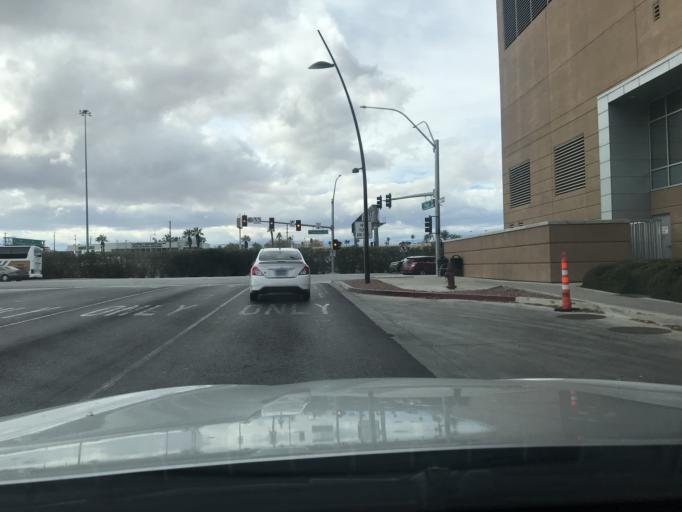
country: US
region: Nevada
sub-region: Clark County
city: Paradise
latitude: 36.1031
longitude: -115.1753
